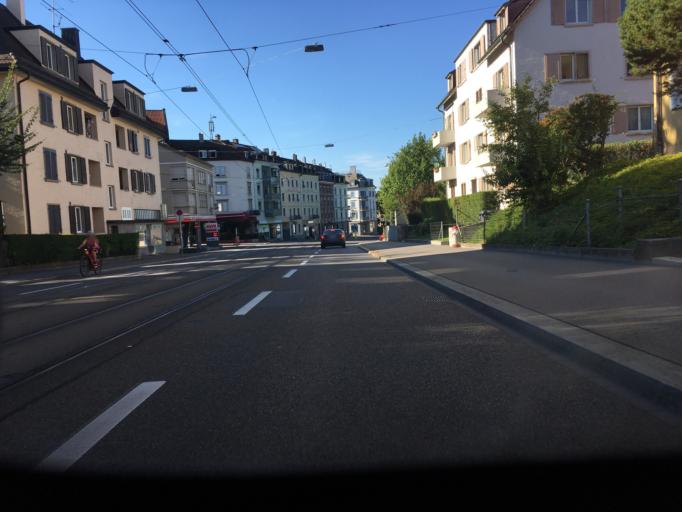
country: CH
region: Zurich
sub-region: Bezirk Zuerich
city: Zuerich (Kreis 2) / Wollishofen
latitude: 47.3391
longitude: 8.5301
